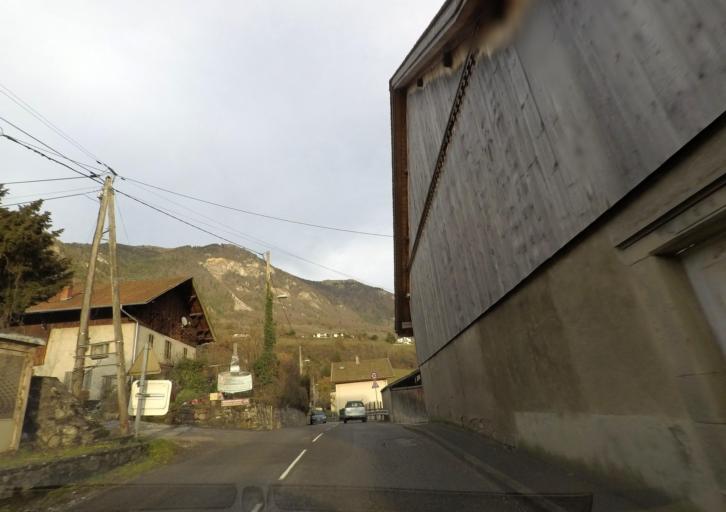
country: FR
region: Rhone-Alpes
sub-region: Departement de la Haute-Savoie
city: Ayse
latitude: 46.0833
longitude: 6.4318
